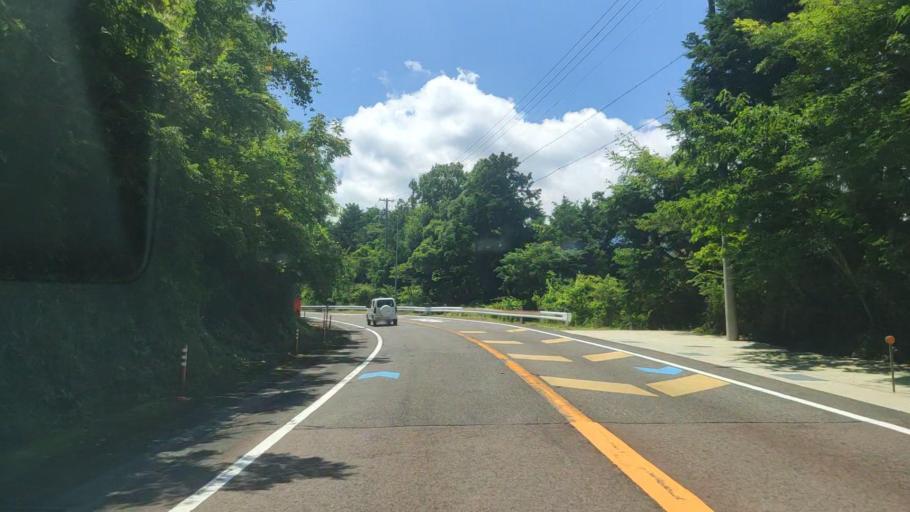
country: JP
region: Mie
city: Owase
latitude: 34.1029
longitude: 136.2031
